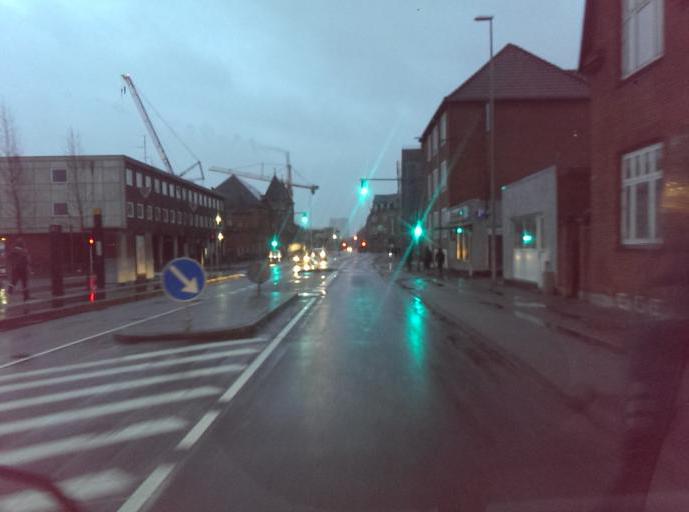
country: DK
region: South Denmark
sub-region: Esbjerg Kommune
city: Esbjerg
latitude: 55.4691
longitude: 8.4583
